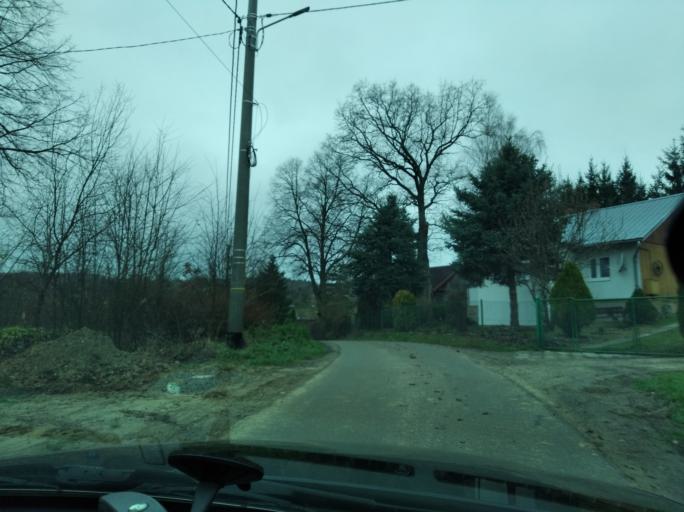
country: PL
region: Subcarpathian Voivodeship
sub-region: Powiat przeworski
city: Jawornik Polski
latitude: 49.9094
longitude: 22.2756
